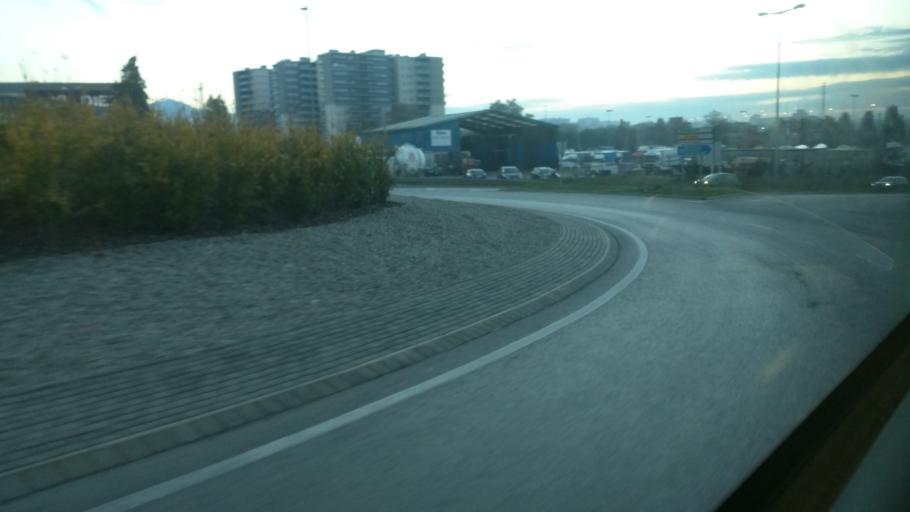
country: ES
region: Catalonia
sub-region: Provincia de Barcelona
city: Sant Feliu de Llobregat
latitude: 41.3741
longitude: 2.0429
